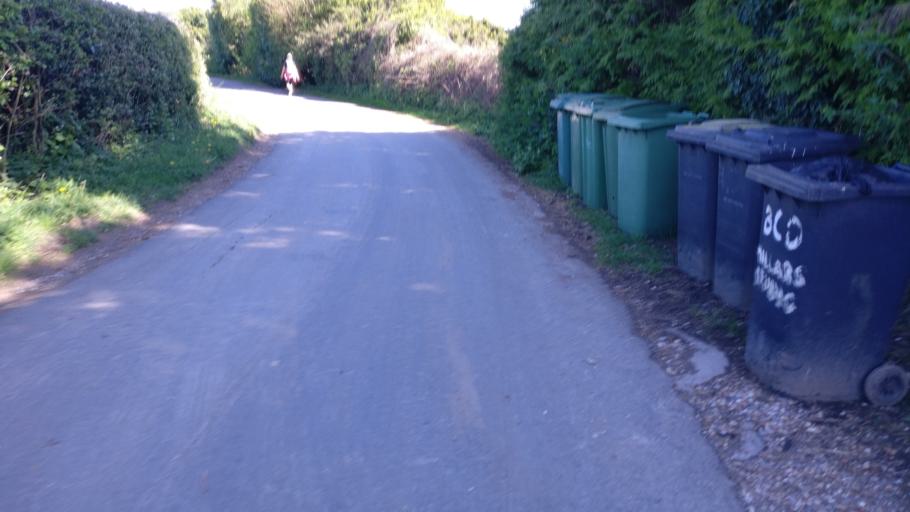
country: GB
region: England
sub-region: Hampshire
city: Basingstoke
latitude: 51.2358
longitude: -1.0858
